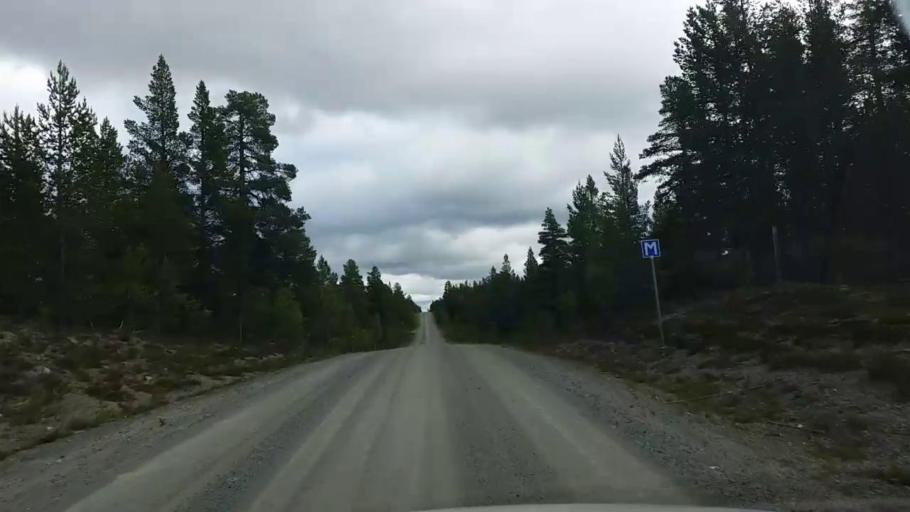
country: NO
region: Hedmark
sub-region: Engerdal
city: Engerdal
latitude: 62.3408
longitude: 12.6122
